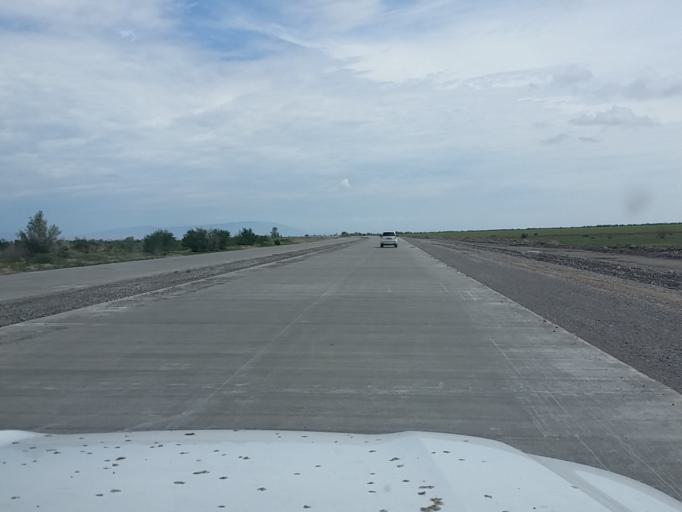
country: KZ
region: Almaty Oblysy
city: Turgen'
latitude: 43.6211
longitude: 78.3649
